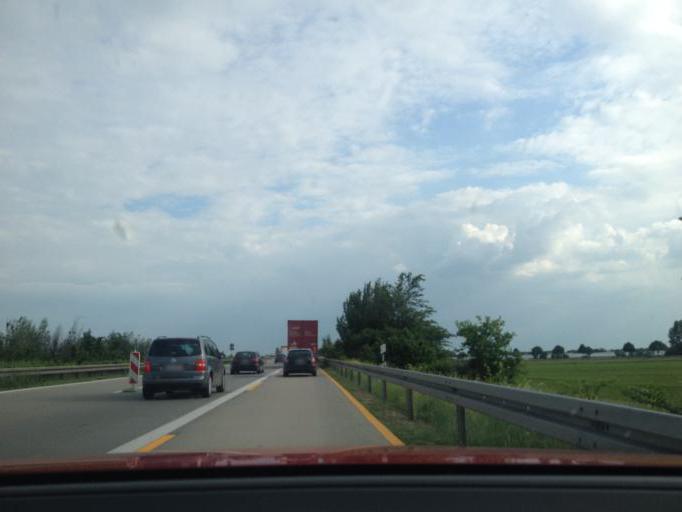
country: DE
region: Saxony-Anhalt
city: Nauendorf
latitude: 51.6059
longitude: 11.8701
